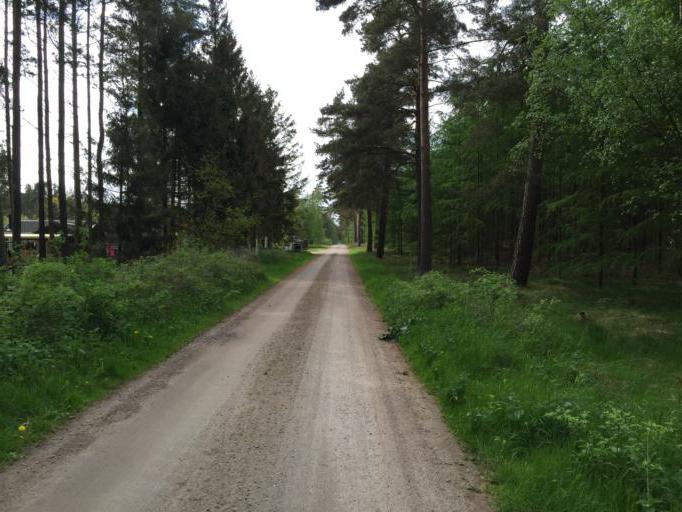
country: SE
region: Skane
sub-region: Sjobo Kommun
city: Sjoebo
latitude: 55.6651
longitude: 13.6373
